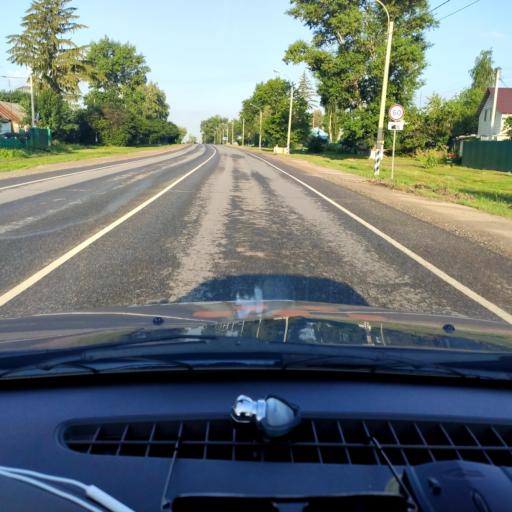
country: RU
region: Lipetsk
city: Kazaki
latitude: 52.5685
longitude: 38.1820
